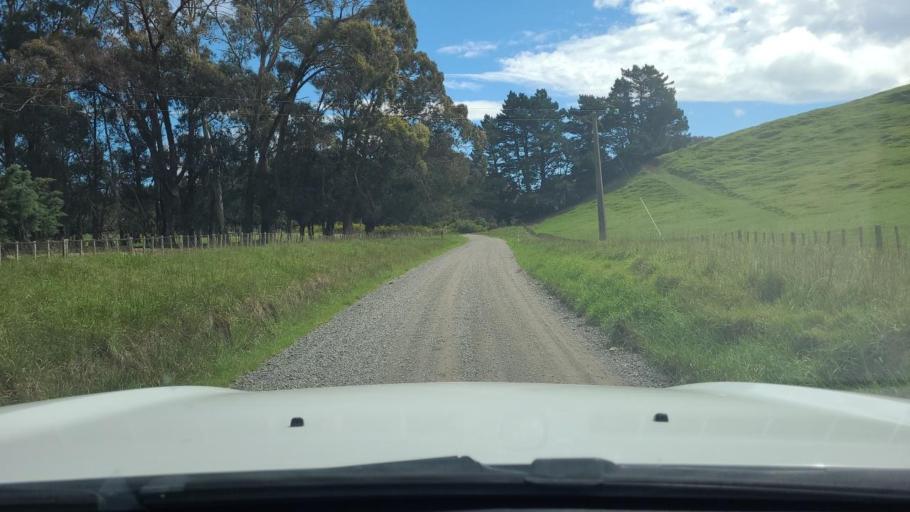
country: NZ
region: Wellington
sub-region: South Wairarapa District
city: Waipawa
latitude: -41.3209
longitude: 175.3783
